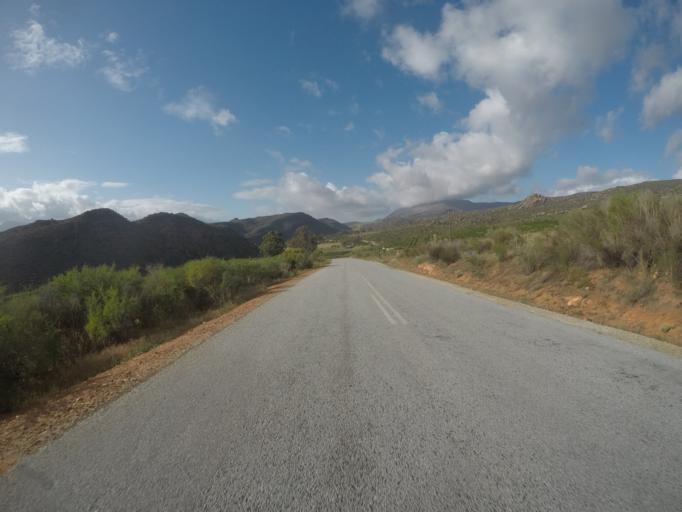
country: ZA
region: Western Cape
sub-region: West Coast District Municipality
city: Clanwilliam
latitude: -32.4300
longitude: 18.9384
